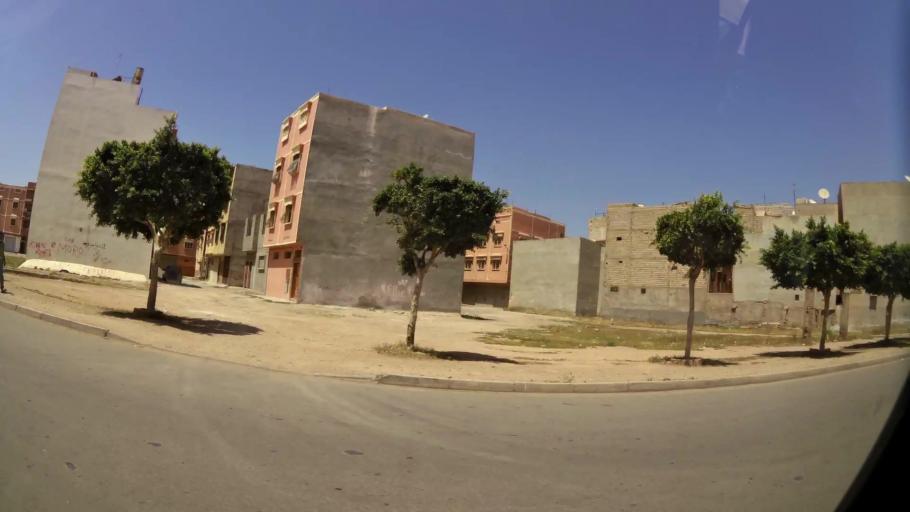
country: MA
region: Souss-Massa-Draa
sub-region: Inezgane-Ait Mellou
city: Inezgane
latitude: 30.3465
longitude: -9.4961
